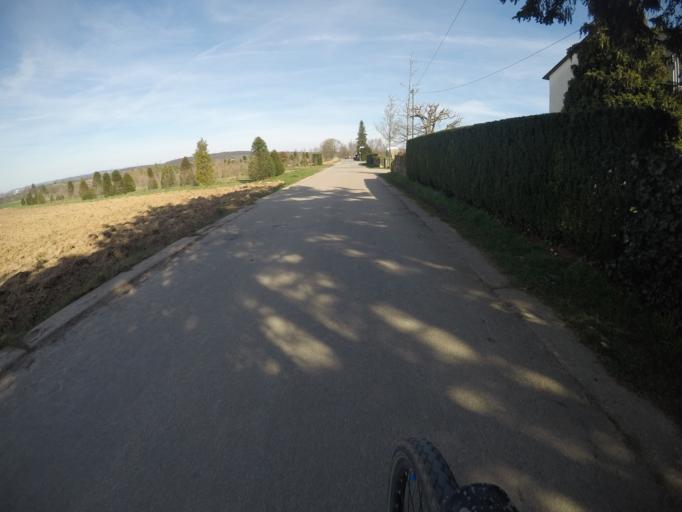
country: DE
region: Baden-Wuerttemberg
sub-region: Regierungsbezirk Stuttgart
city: Stuttgart Muehlhausen
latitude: 48.8417
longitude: 9.2487
